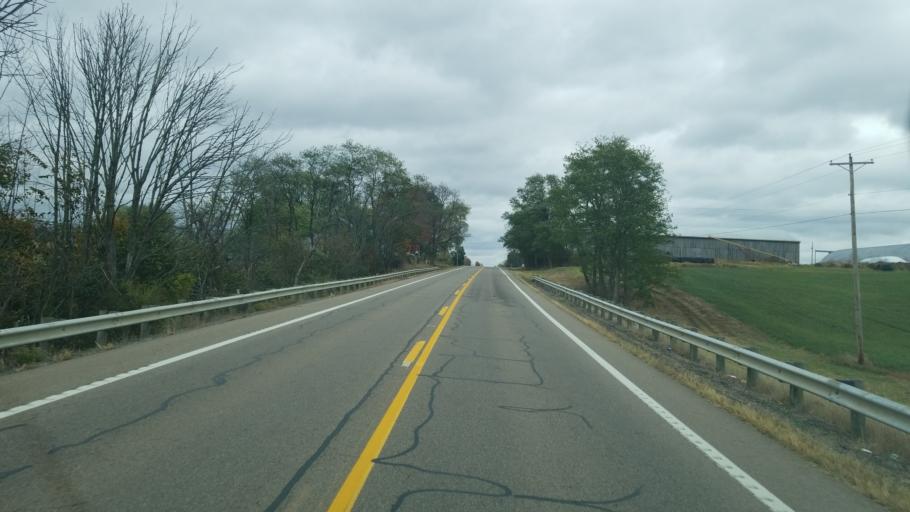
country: US
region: Ohio
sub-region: Licking County
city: Utica
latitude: 40.2704
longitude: -82.3725
